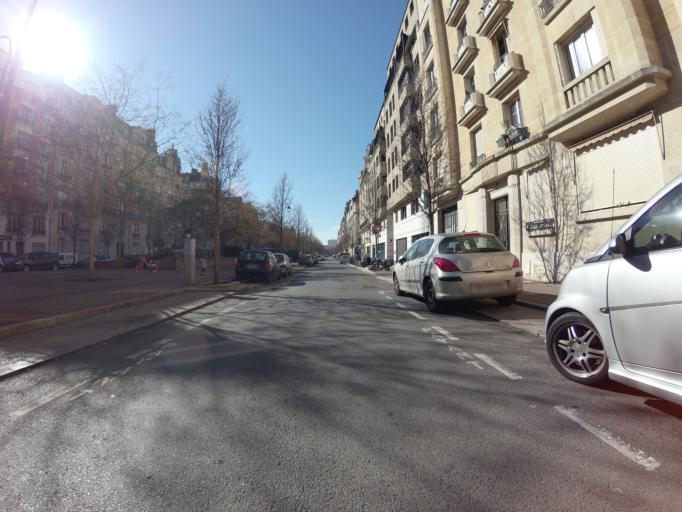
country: FR
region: Ile-de-France
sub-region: Departement des Hauts-de-Seine
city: Clichy
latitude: 48.9030
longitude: 2.3106
